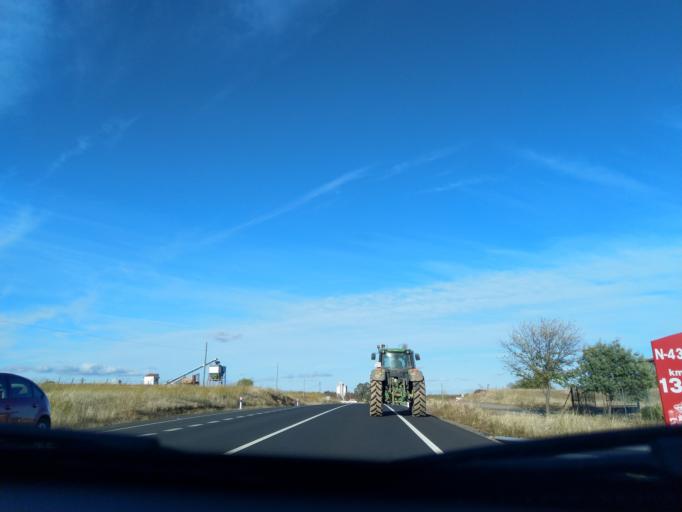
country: ES
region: Extremadura
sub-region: Provincia de Badajoz
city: Ahillones
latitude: 38.2717
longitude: -5.8340
